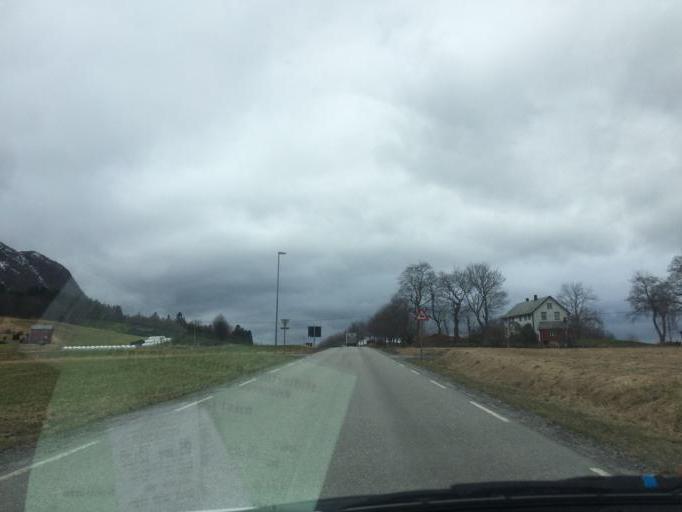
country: NO
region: More og Romsdal
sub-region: Gjemnes
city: Batnfjordsora
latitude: 62.9638
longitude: 7.7661
